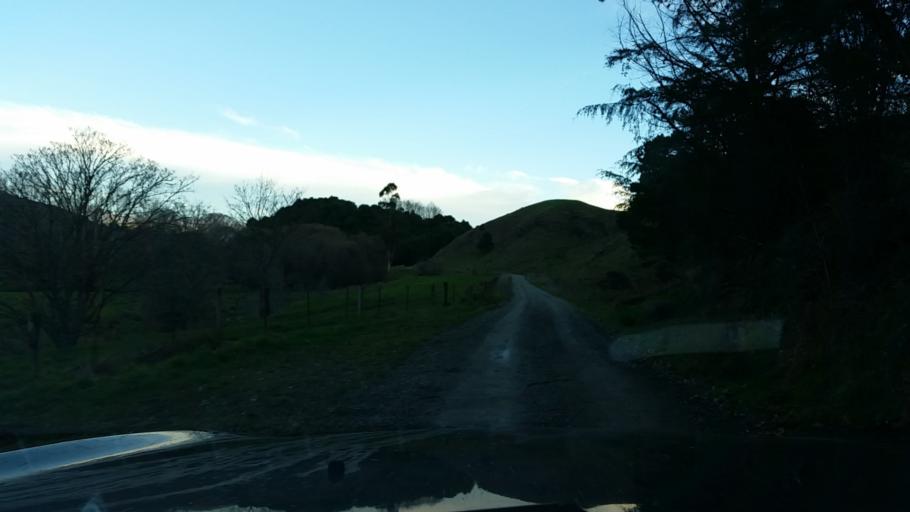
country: NZ
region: Marlborough
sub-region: Marlborough District
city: Blenheim
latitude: -41.5010
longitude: 173.5900
